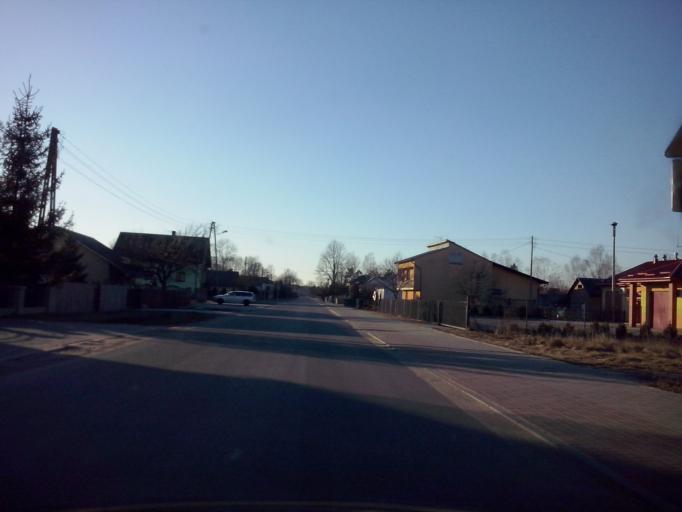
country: PL
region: Subcarpathian Voivodeship
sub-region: Powiat nizanski
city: Harasiuki
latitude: 50.4732
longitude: 22.4845
